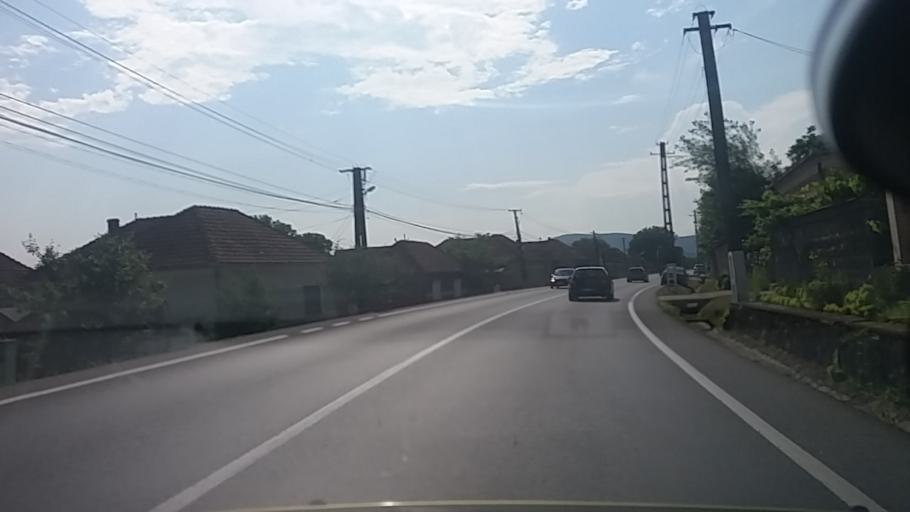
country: RO
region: Arad
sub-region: Comuna Barzava
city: Barzava
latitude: 46.1062
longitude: 21.9904
